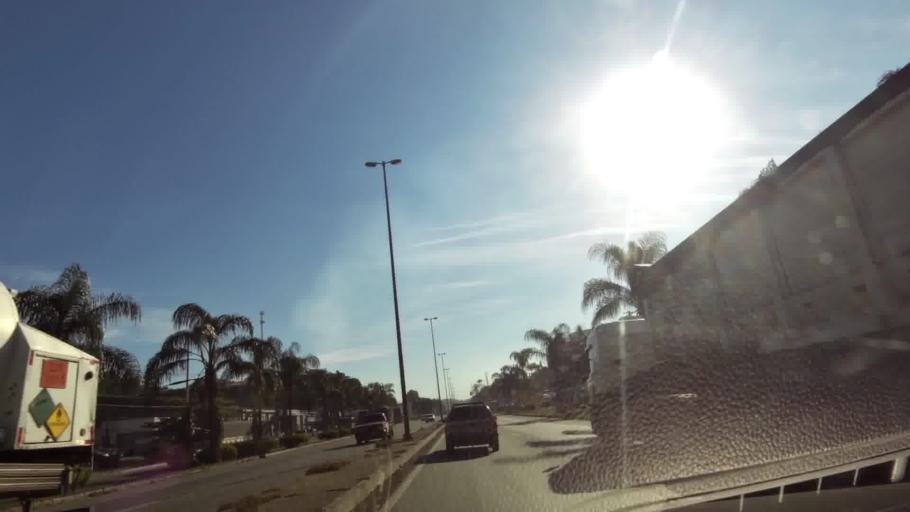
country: BR
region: Espirito Santo
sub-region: Viana
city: Viana
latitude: -20.3554
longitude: -40.4175
